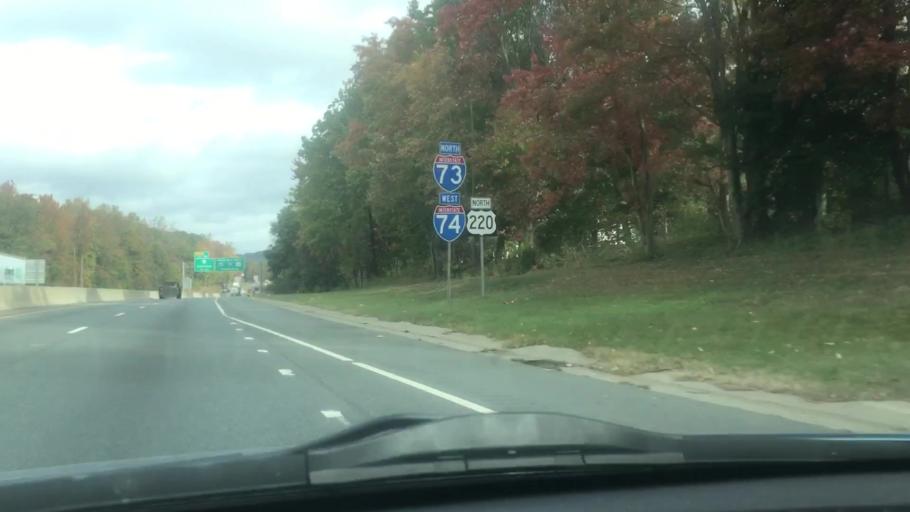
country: US
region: North Carolina
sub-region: Randolph County
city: Asheboro
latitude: 35.6927
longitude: -79.8322
